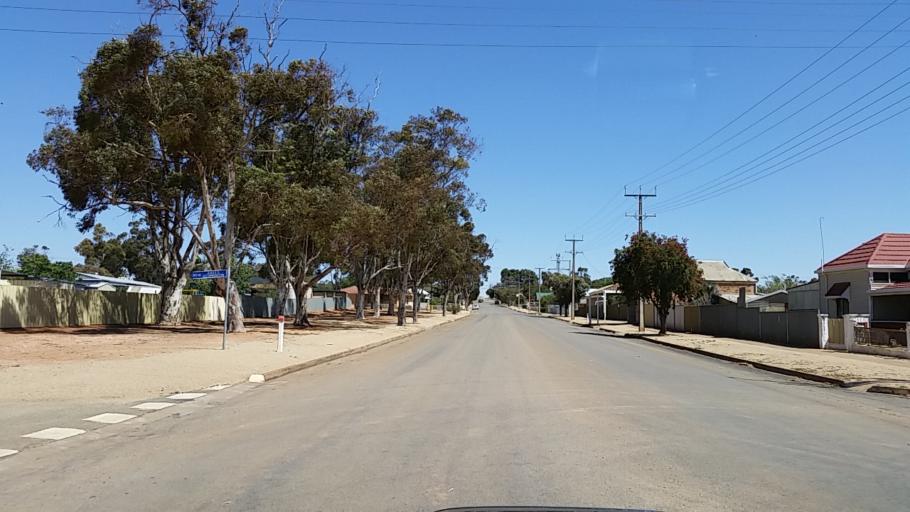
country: AU
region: South Australia
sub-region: Peterborough
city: Peterborough
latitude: -32.9761
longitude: 138.8318
